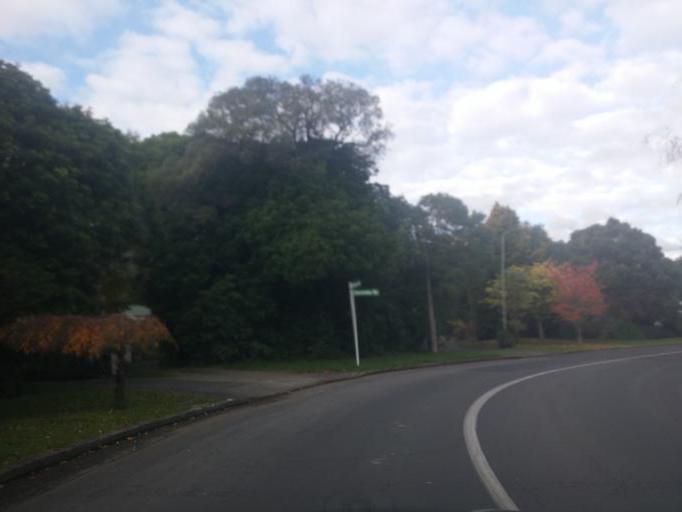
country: NZ
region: Wellington
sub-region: Kapiti Coast District
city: Paraparaumu
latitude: -40.8766
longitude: 175.0607
